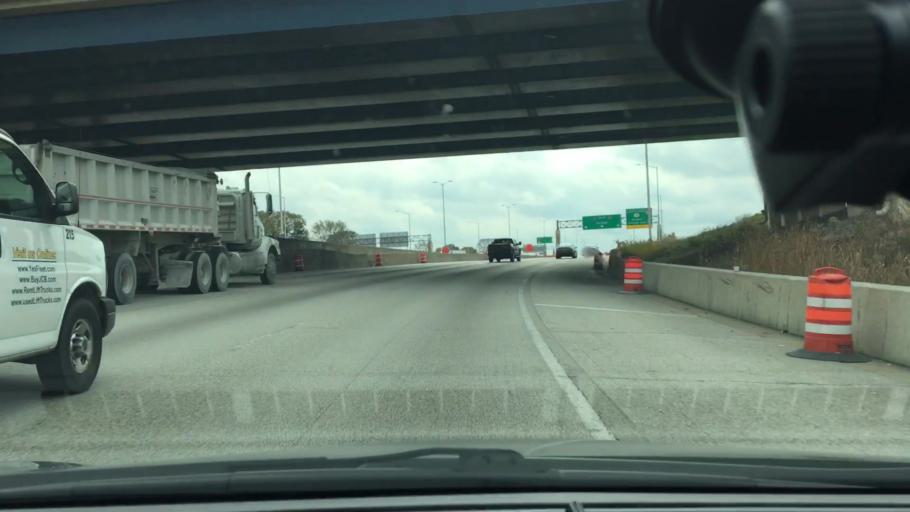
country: US
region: Wisconsin
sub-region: Milwaukee County
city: Saint Francis
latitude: 42.9596
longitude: -87.9346
